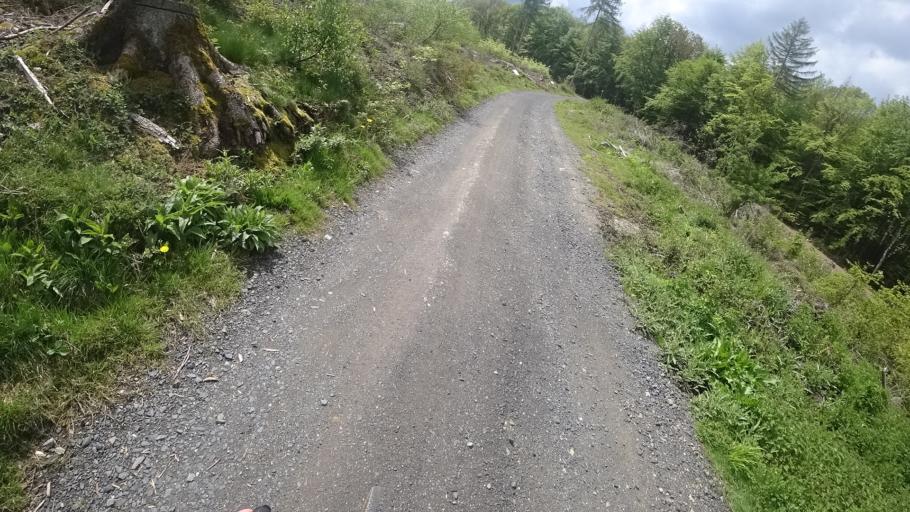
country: DE
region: Rheinland-Pfalz
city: Scheuerfeld
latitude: 50.7791
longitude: 7.8427
